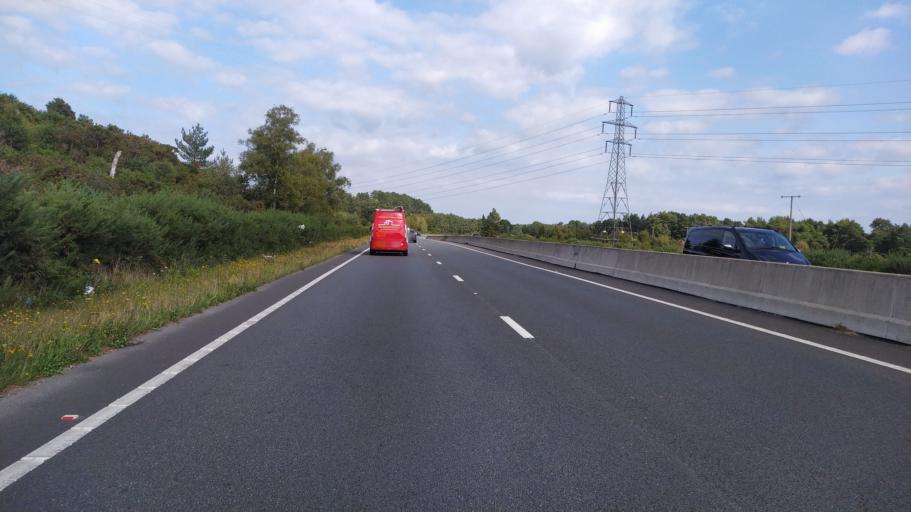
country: GB
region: England
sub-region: Dorset
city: St Leonards
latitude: 50.7975
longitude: -1.8156
